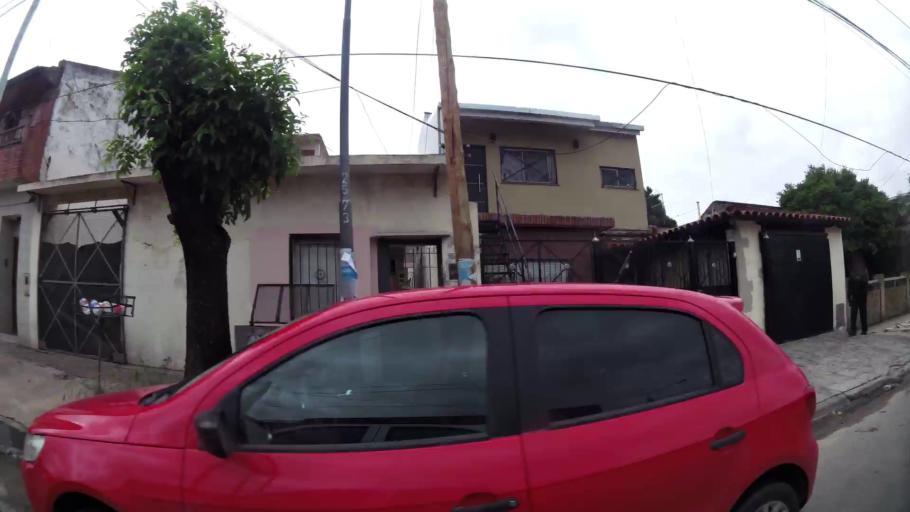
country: AR
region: Buenos Aires
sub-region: Partido de Lanus
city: Lanus
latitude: -34.7297
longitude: -58.3712
